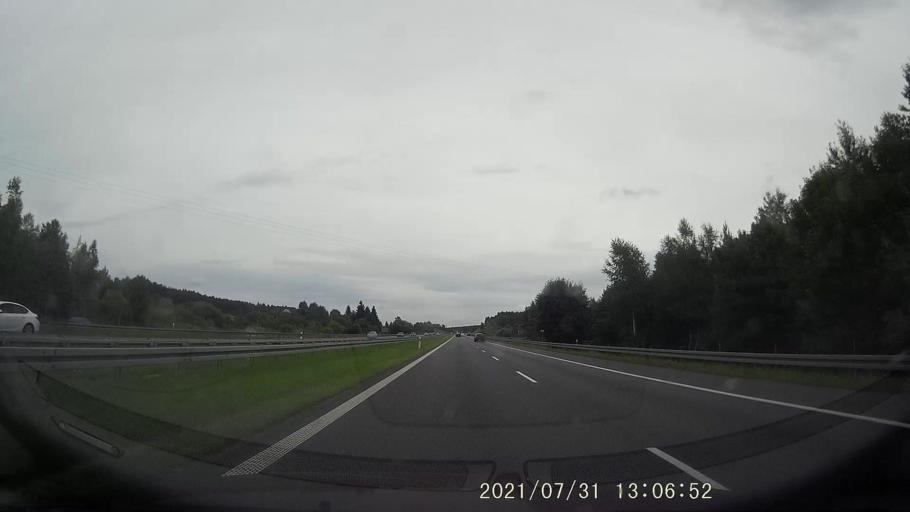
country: PL
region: Lesser Poland Voivodeship
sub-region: Powiat chrzanowski
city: Balin
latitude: 50.1515
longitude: 19.3472
